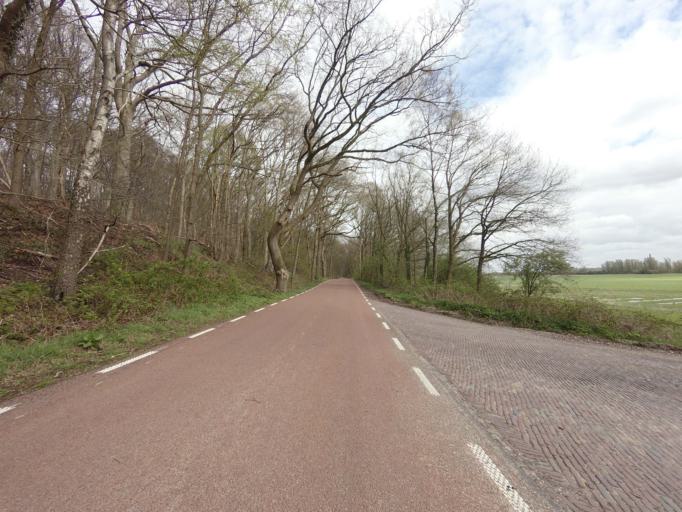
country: NL
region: Gelderland
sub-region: Gemeente Renkum
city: Heelsum
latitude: 51.9700
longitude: 5.7712
